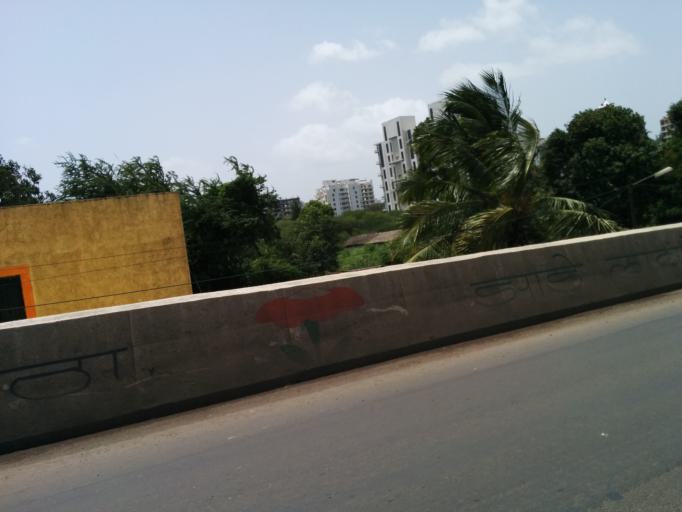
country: IN
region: Maharashtra
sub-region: Pune Division
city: Lohogaon
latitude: 18.5252
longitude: 73.9322
